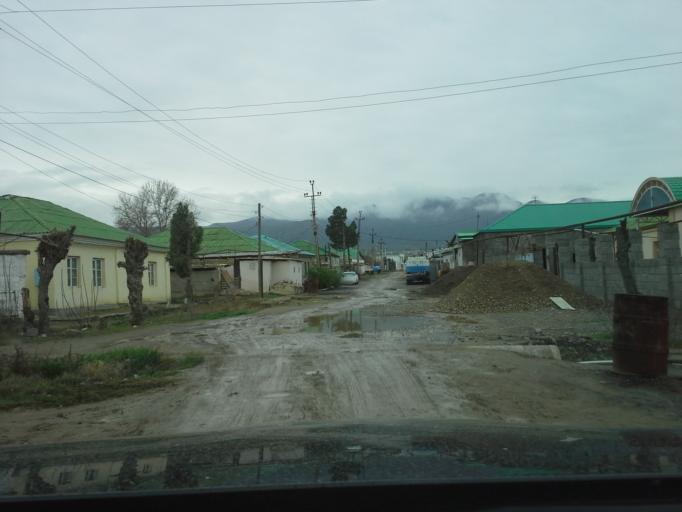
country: TM
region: Ahal
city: Abadan
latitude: 37.9638
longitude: 58.2266
